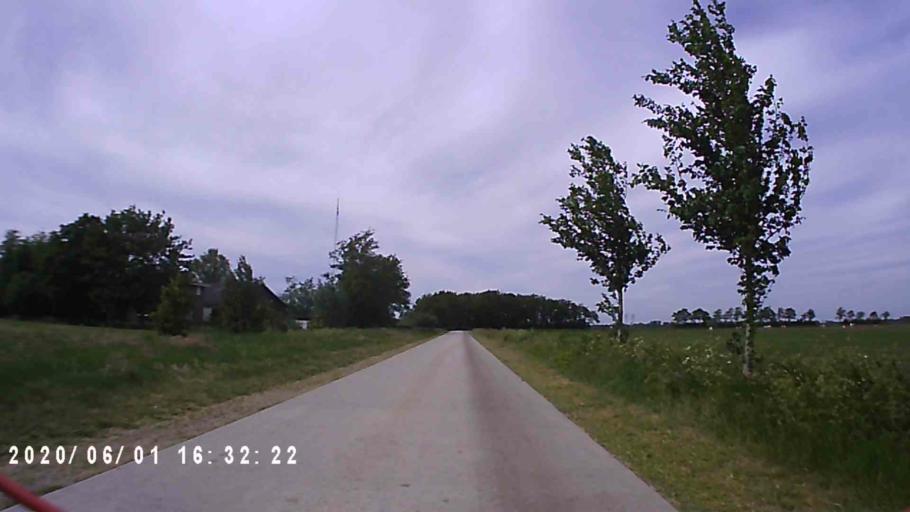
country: NL
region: Friesland
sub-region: Gemeente Leeuwarden
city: Camminghaburen
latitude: 53.1894
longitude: 5.8647
